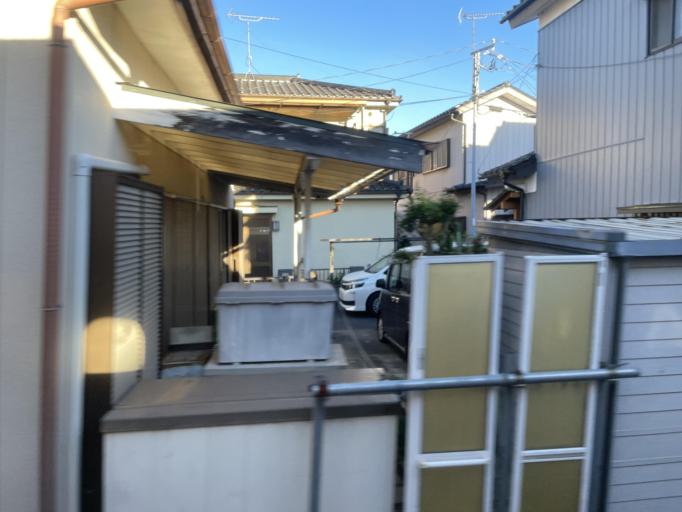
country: JP
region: Saitama
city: Satte
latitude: 36.0822
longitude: 139.7158
